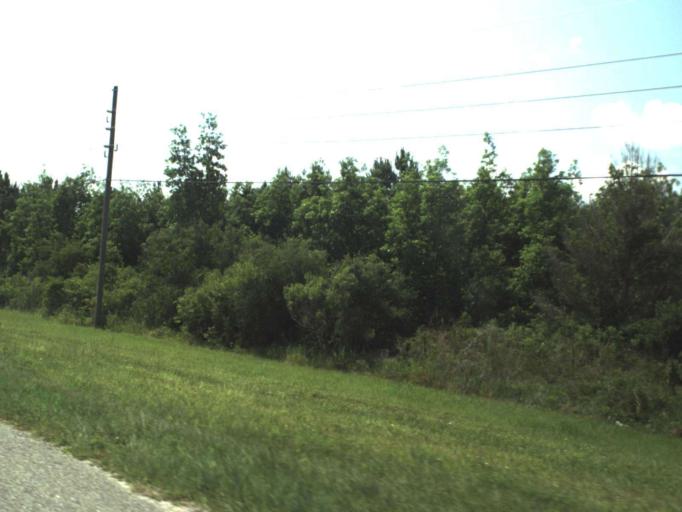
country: US
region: Florida
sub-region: Volusia County
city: Samsula-Spruce Creek
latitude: 29.0156
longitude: -81.0951
